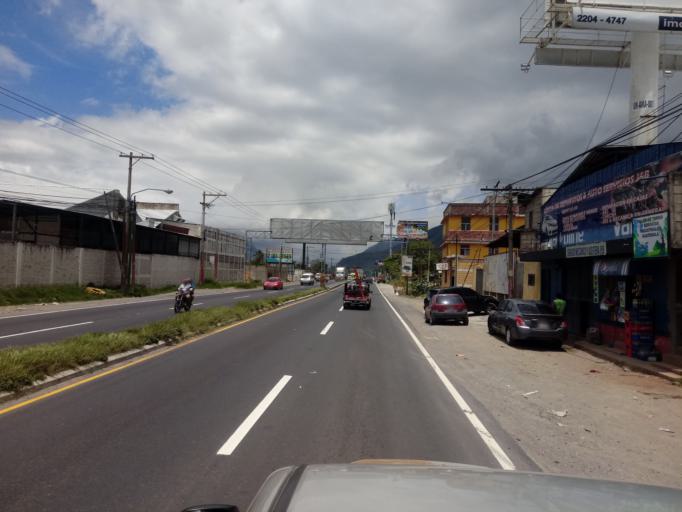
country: GT
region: Guatemala
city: Amatitlan
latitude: 14.4802
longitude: -90.6307
